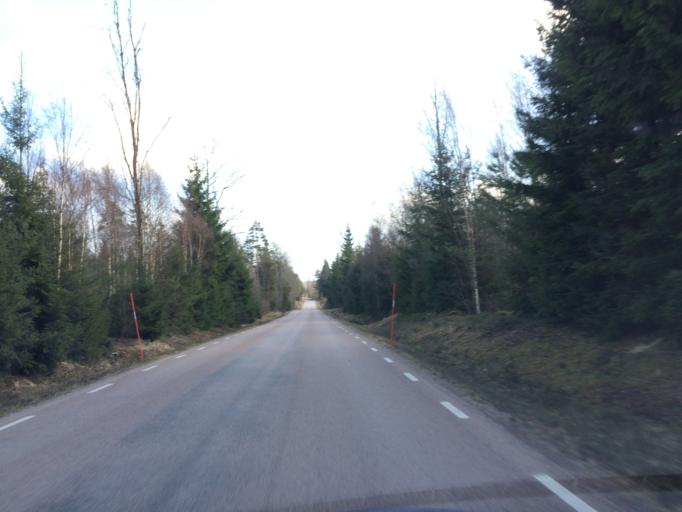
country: SE
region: Kronoberg
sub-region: Ljungby Kommun
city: Ljungby
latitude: 56.6678
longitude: 13.9012
